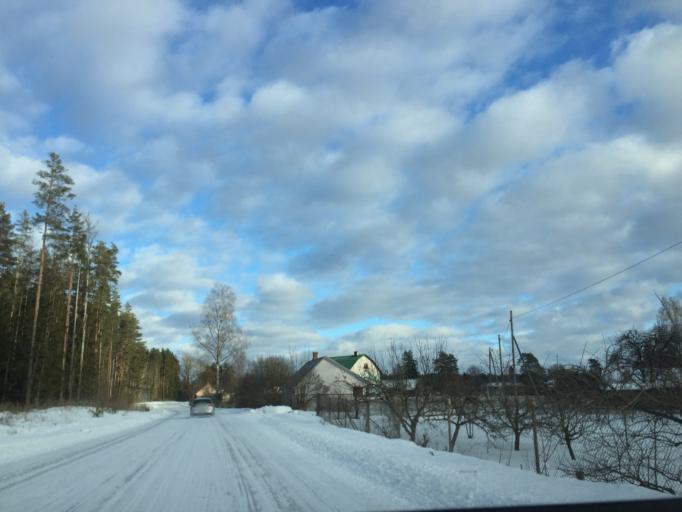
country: LV
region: Ogre
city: Jumprava
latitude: 56.5641
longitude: 24.9207
